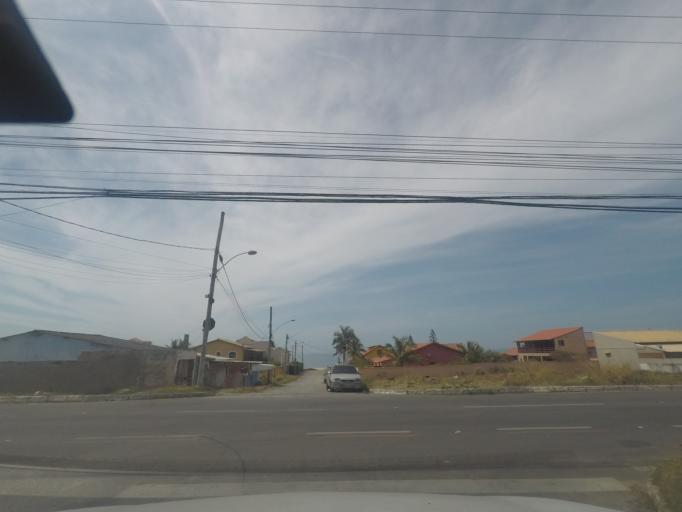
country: BR
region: Rio de Janeiro
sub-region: Marica
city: Marica
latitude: -22.9562
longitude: -42.7496
